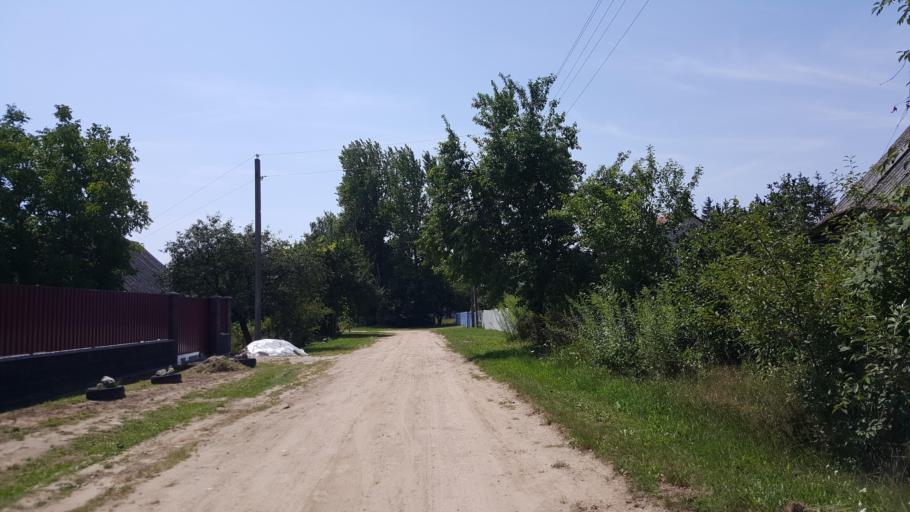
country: BY
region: Brest
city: Vysokaye
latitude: 52.3597
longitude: 23.4021
